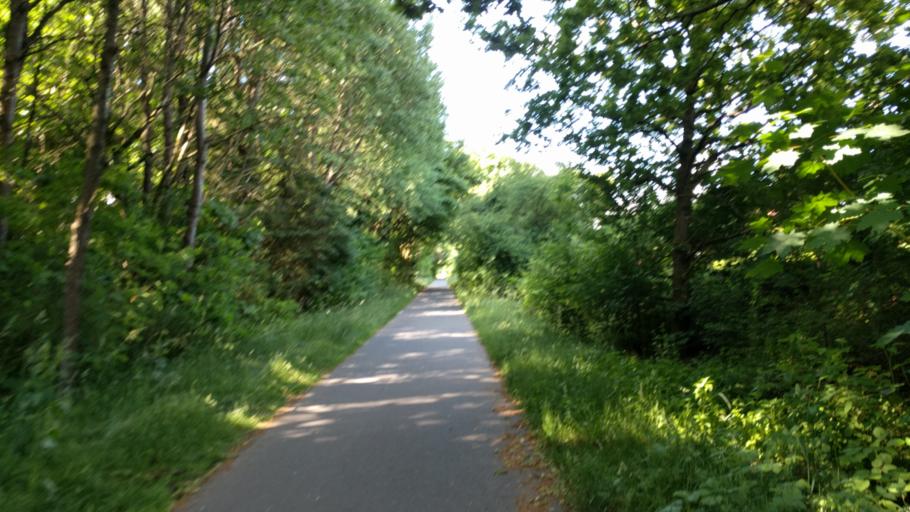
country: DK
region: Central Jutland
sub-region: Viborg Kommune
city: Viborg
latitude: 56.4259
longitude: 9.3853
